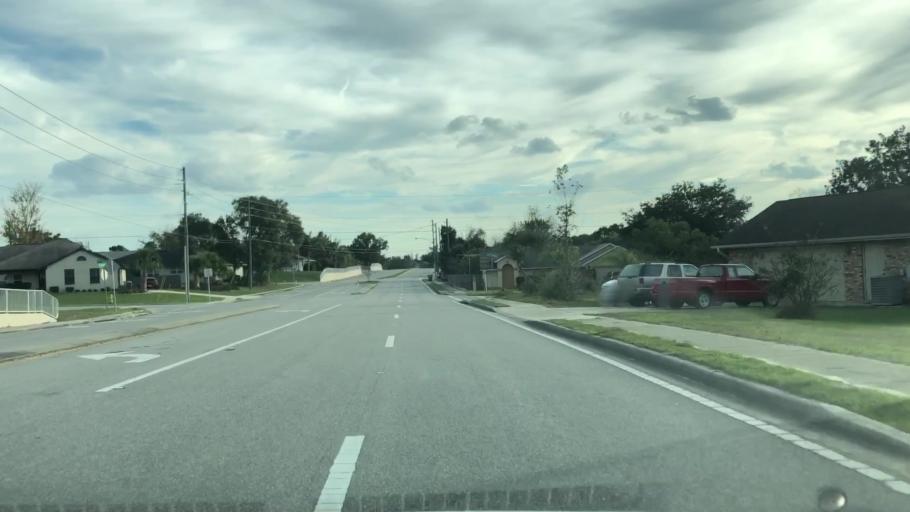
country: US
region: Florida
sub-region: Volusia County
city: Deltona
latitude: 28.9303
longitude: -81.2612
